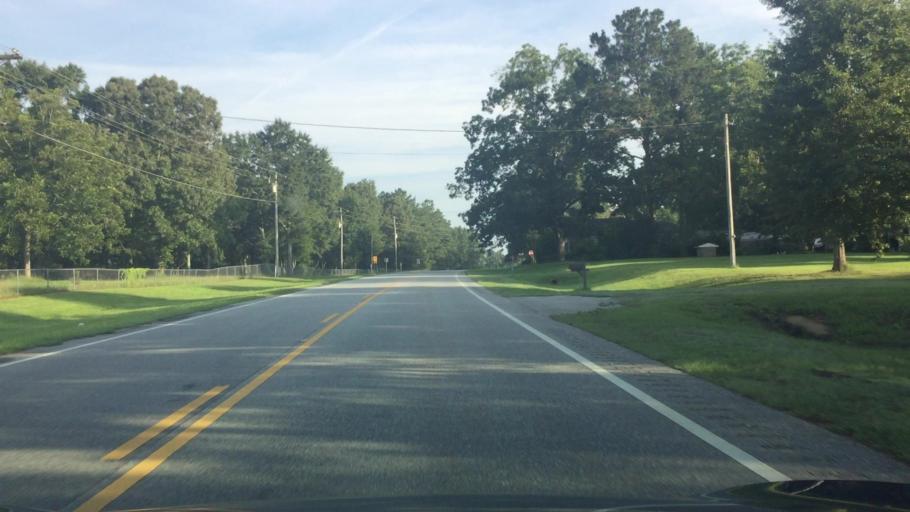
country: US
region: Alabama
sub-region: Covington County
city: Andalusia
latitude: 31.2588
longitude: -86.4698
